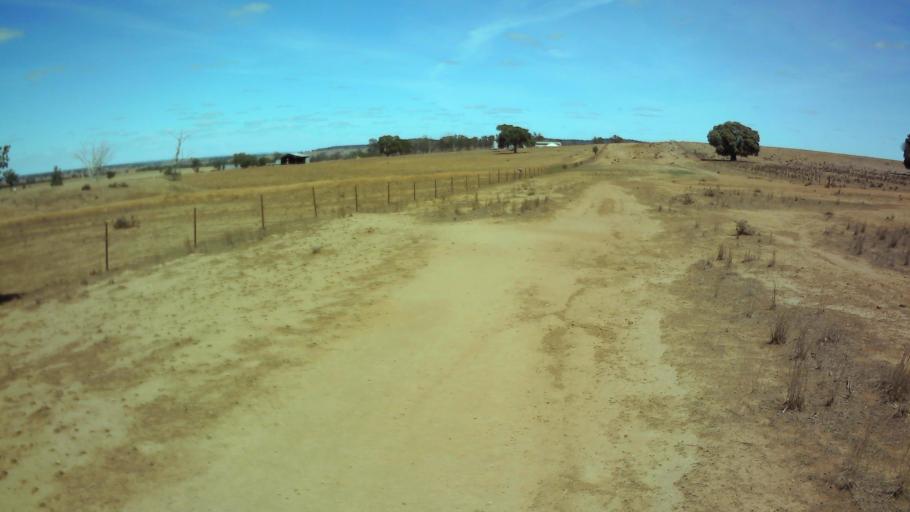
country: AU
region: New South Wales
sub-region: Forbes
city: Forbes
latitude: -33.7179
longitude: 147.8185
